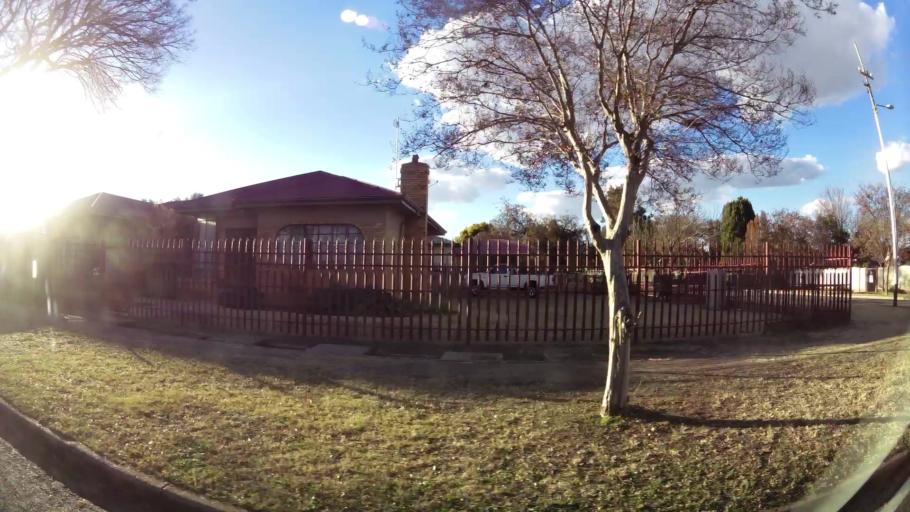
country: ZA
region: North-West
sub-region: Dr Kenneth Kaunda District Municipality
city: Potchefstroom
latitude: -26.7241
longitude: 27.0921
